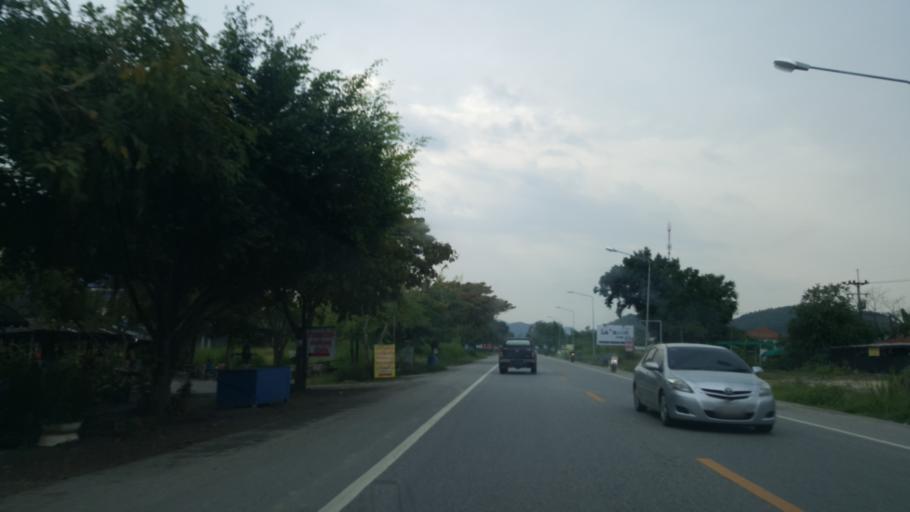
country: TH
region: Rayong
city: Ban Chang
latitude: 12.7272
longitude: 100.9740
